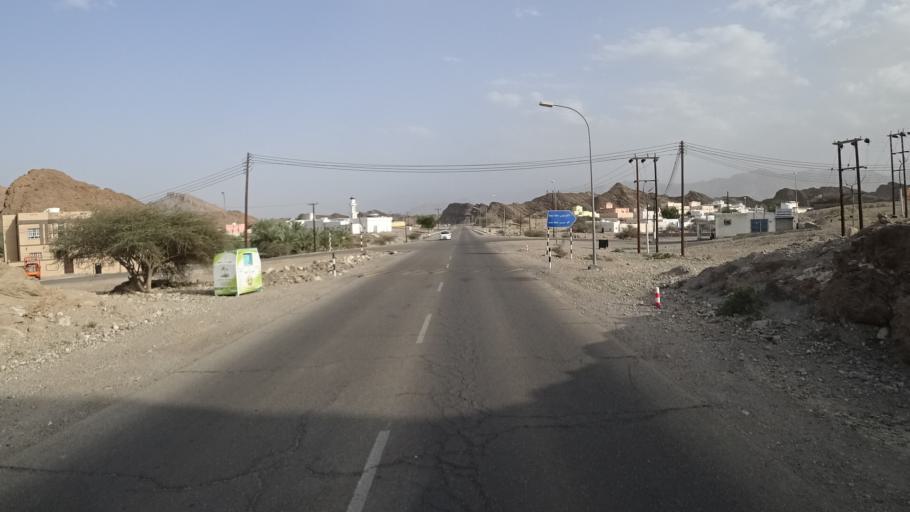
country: OM
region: Muhafazat Masqat
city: Bawshar
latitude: 23.3766
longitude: 58.5151
